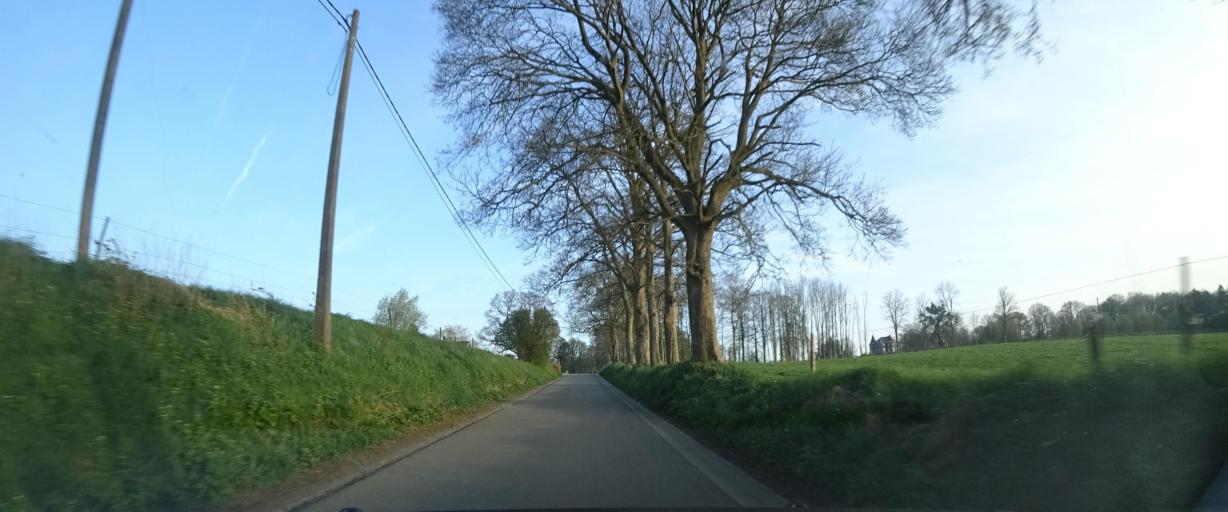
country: BE
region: Wallonia
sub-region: Province de Namur
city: Hamois
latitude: 50.3149
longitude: 5.1535
